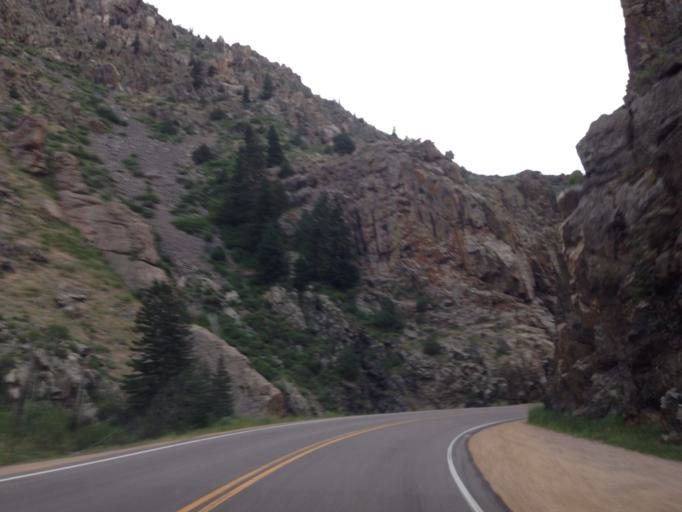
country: US
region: Colorado
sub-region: Larimer County
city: Laporte
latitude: 40.6942
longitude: -105.3762
